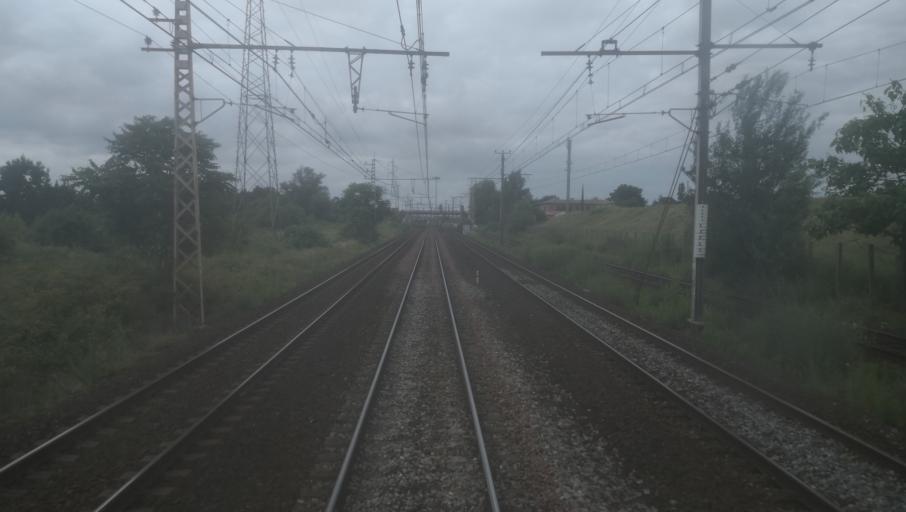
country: FR
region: Midi-Pyrenees
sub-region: Departement de la Haute-Garonne
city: Fenouillet
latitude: 43.6816
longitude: 1.4031
